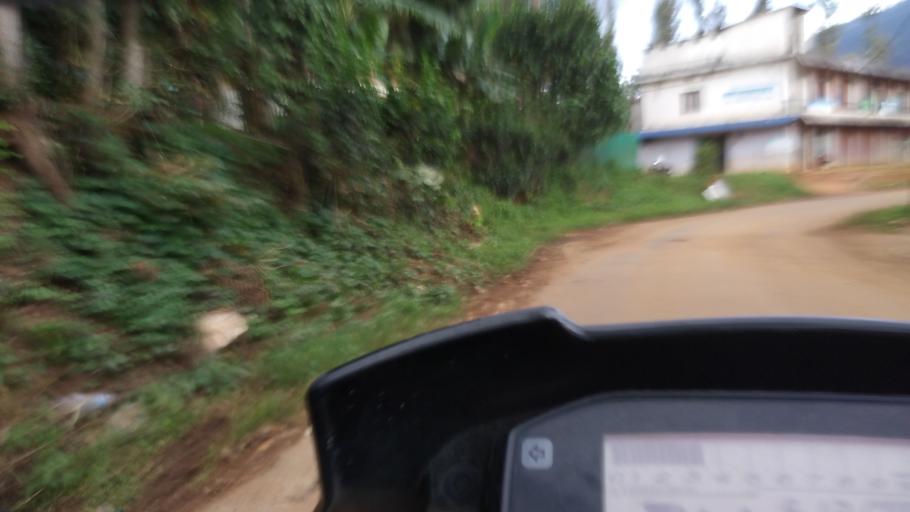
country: IN
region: Tamil Nadu
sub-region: Theni
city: Bodinayakkanur
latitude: 10.0244
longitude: 77.2393
